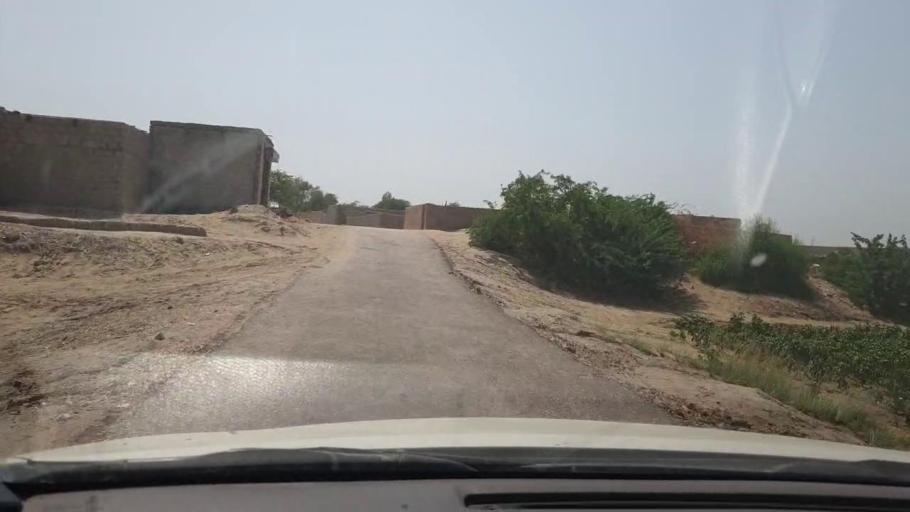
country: PK
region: Sindh
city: Rohri
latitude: 27.5225
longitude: 69.0587
